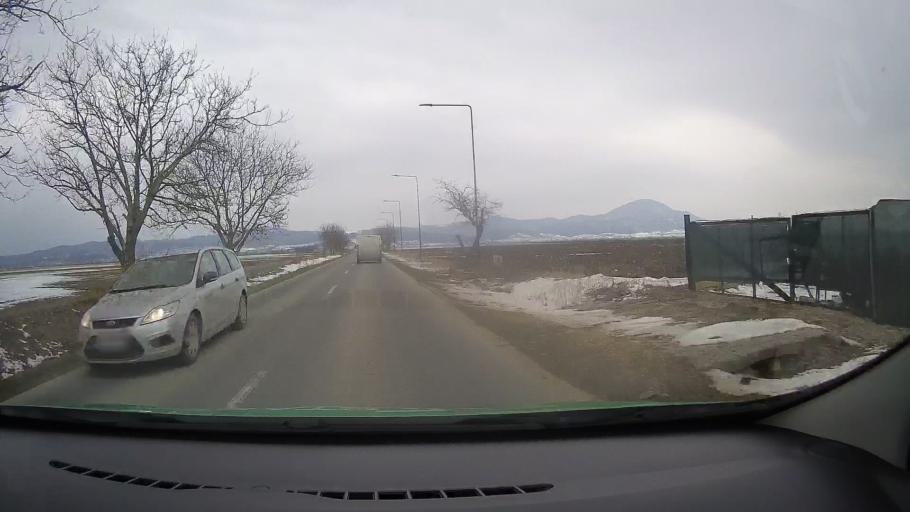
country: RO
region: Brasov
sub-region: Comuna Cristian
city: Cristian
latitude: 45.6320
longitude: 25.4598
